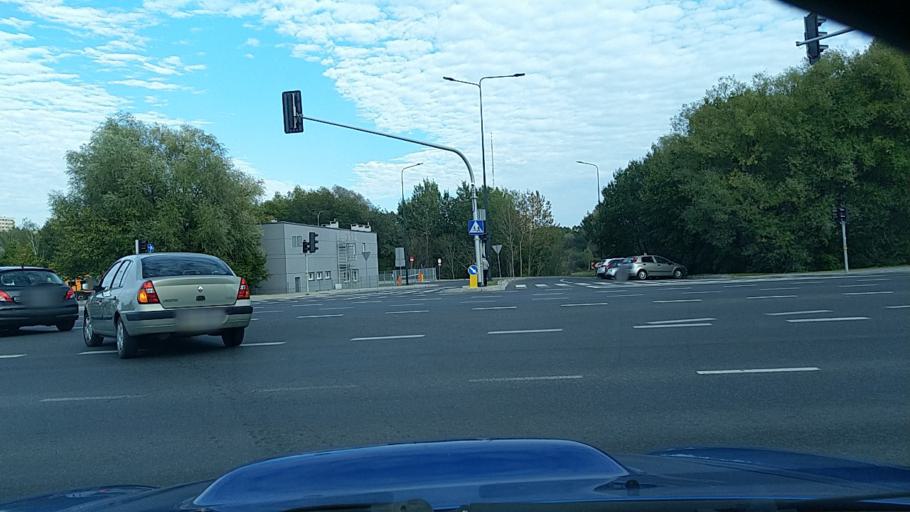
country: PL
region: Warmian-Masurian Voivodeship
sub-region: Olsztyn
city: Kortowo
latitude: 53.7498
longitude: 20.4862
